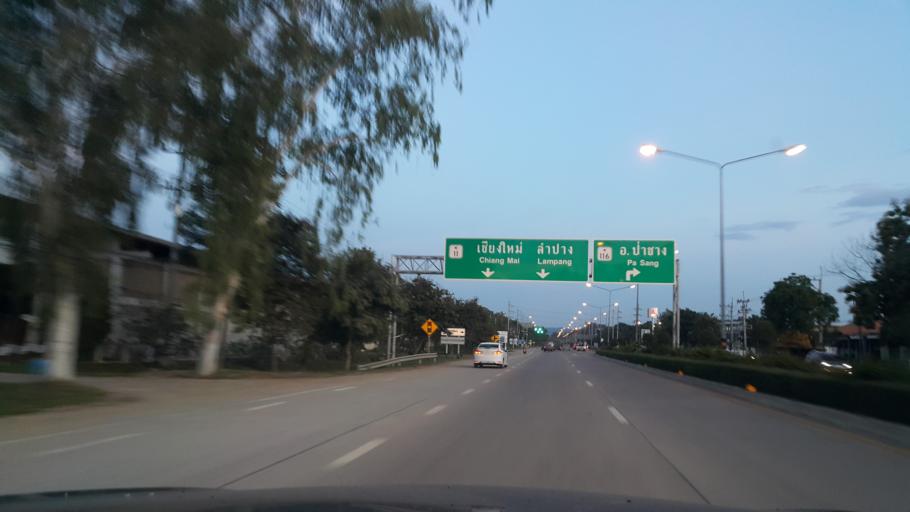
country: TH
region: Lamphun
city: Lamphun
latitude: 18.5580
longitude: 99.0395
